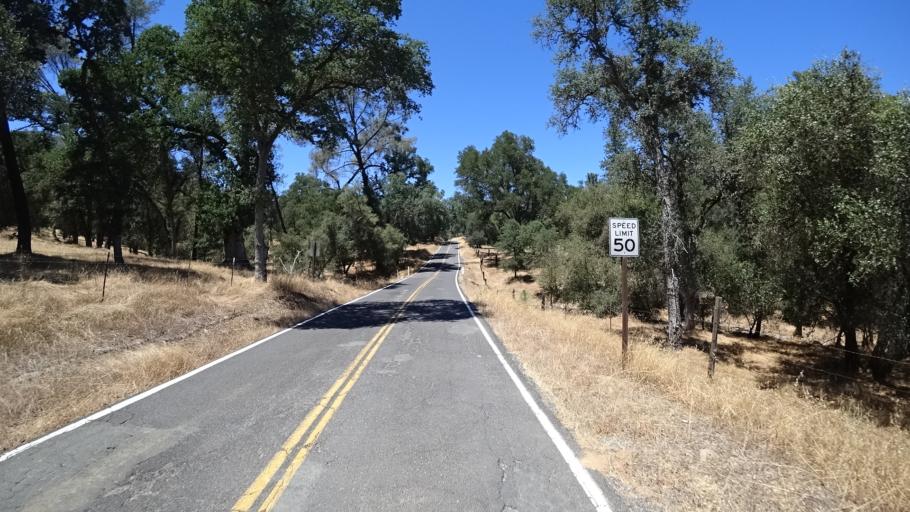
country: US
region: California
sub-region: Calaveras County
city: San Andreas
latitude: 38.1275
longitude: -120.6620
